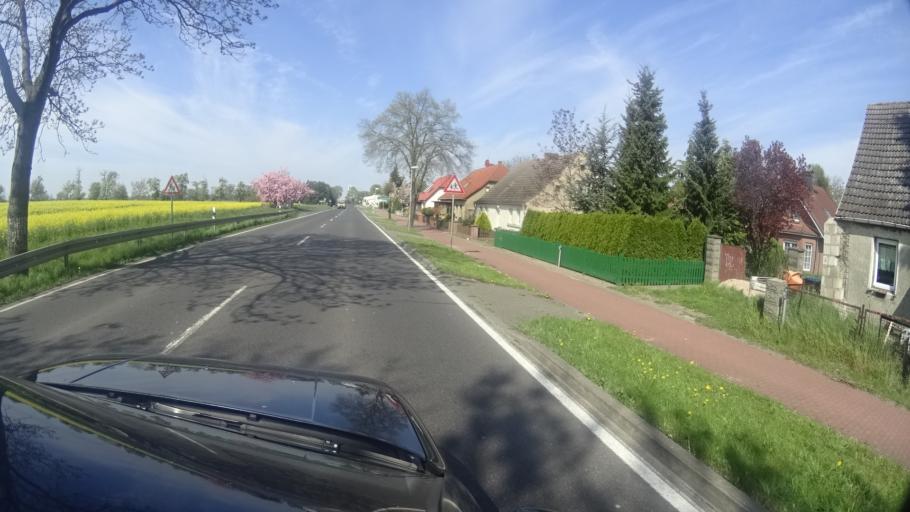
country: DE
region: Brandenburg
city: Retzow
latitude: 52.6325
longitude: 12.7170
